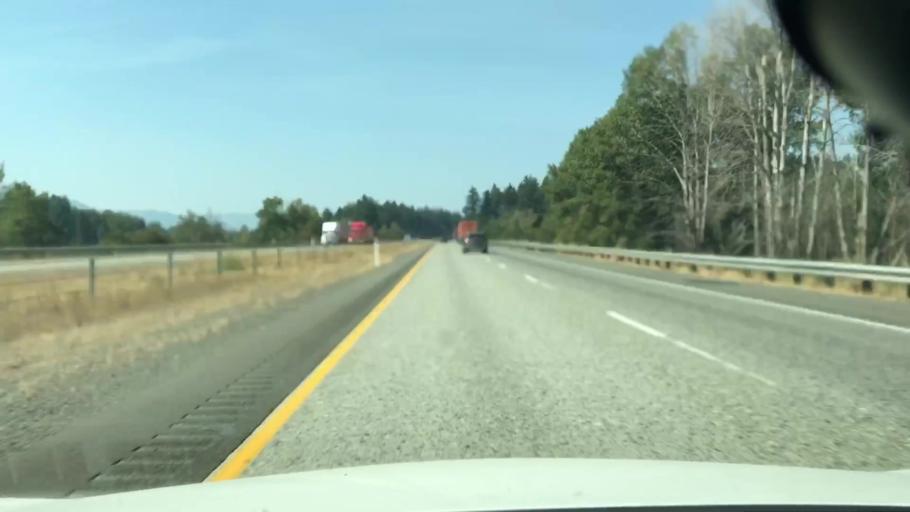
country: US
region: Washington
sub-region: Kittitas County
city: Cle Elum
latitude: 47.1924
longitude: -120.9432
